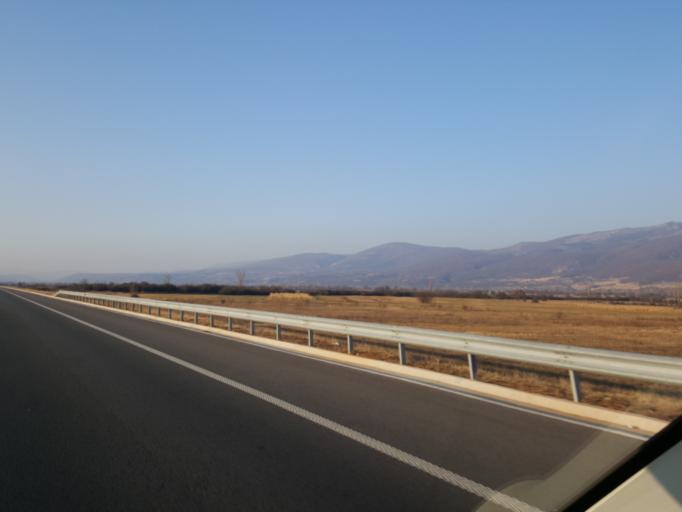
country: RS
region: Central Serbia
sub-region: Pirotski Okrug
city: Pirot
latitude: 43.0807
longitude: 22.6639
